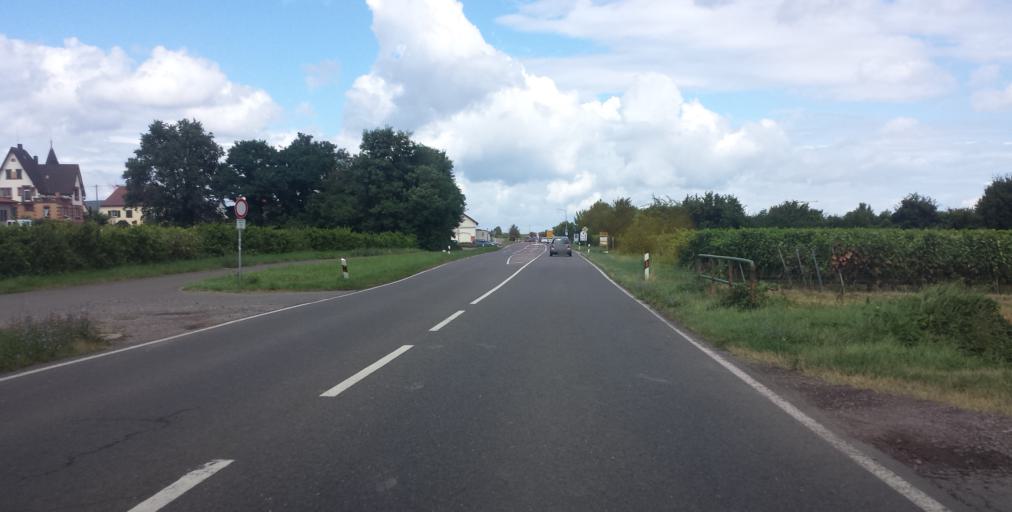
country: DE
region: Rheinland-Pfalz
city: Maikammer
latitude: 49.3021
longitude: 8.1414
